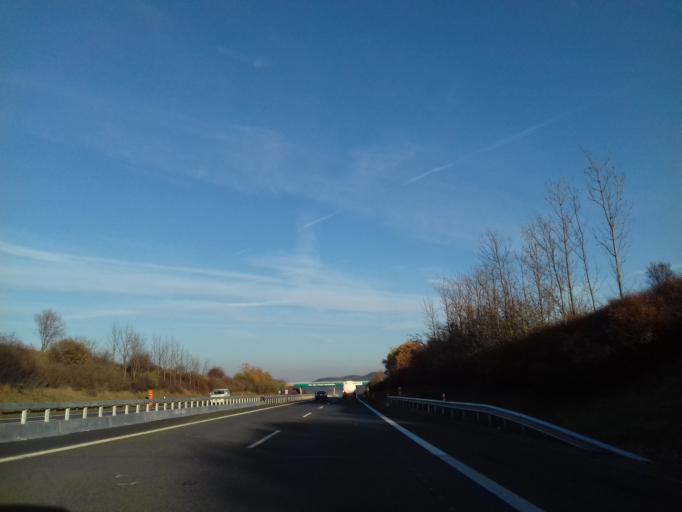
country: CZ
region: Central Bohemia
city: Zebrak
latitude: 49.8899
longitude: 13.9295
